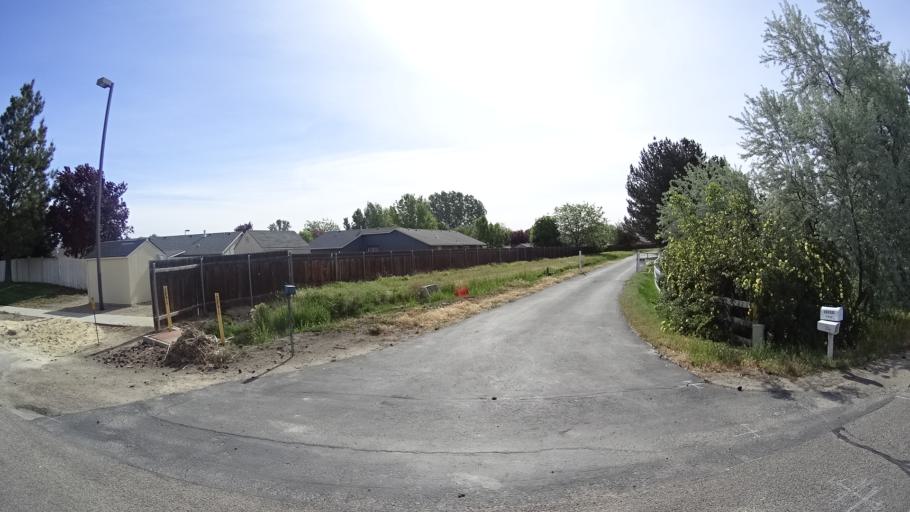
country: US
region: Idaho
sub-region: Ada County
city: Meridian
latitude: 43.5529
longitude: -116.3343
